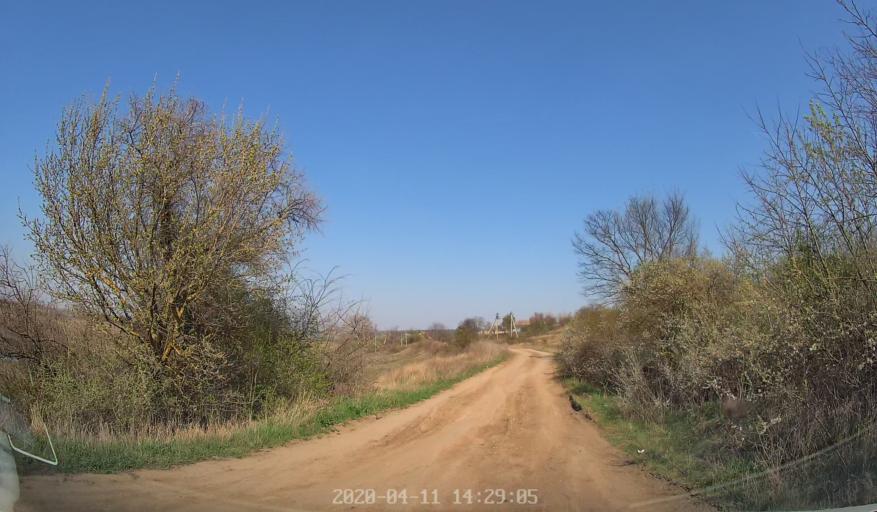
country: MD
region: Chisinau
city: Vadul lui Voda
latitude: 47.0978
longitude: 29.1548
